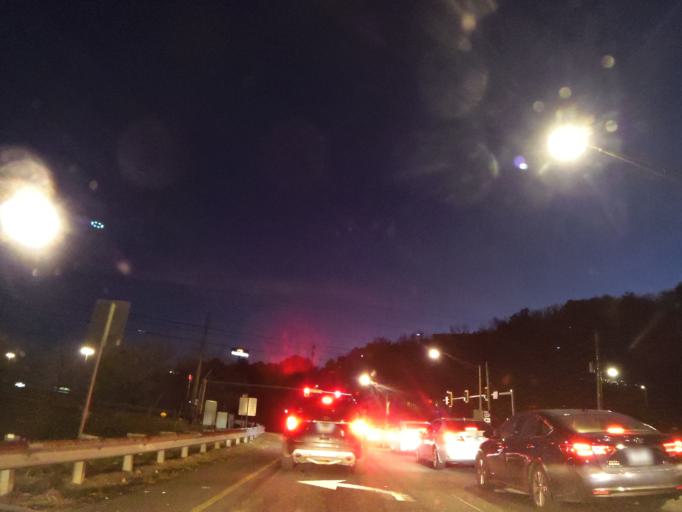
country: US
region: Georgia
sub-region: Whitfield County
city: Dalton
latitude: 34.7616
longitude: -85.0028
